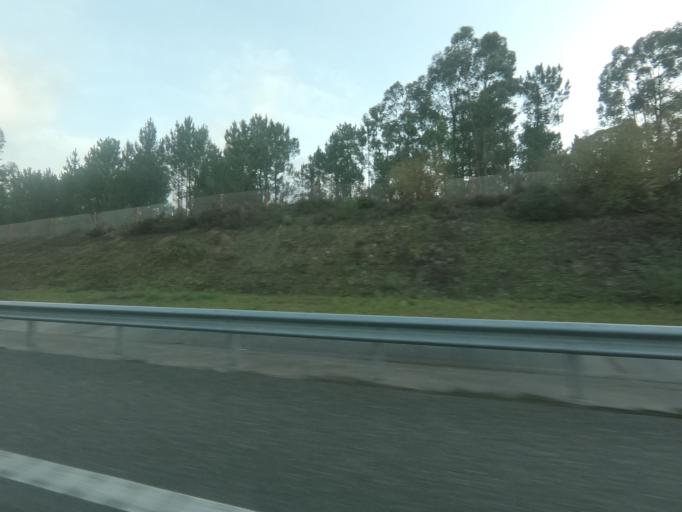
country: ES
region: Galicia
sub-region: Provincia de Pontevedra
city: Tui
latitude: 42.1032
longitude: -8.6451
